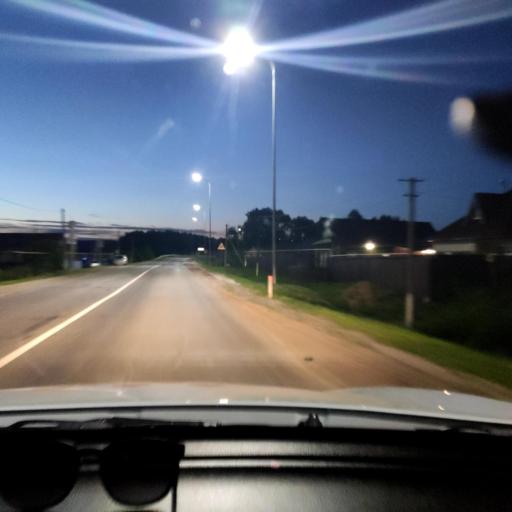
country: RU
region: Tatarstan
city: Rybnaya Sloboda
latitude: 55.4733
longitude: 50.0248
